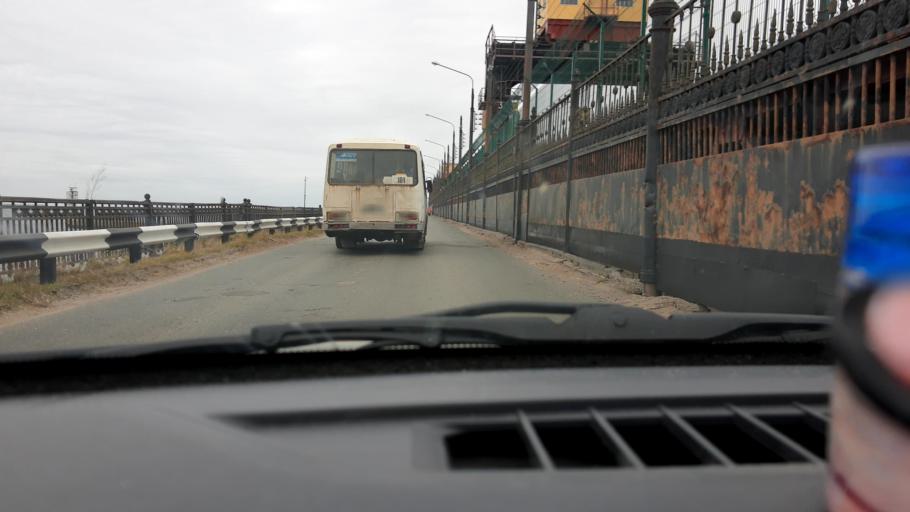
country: RU
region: Nizjnij Novgorod
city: Zavolzh'ye
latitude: 56.6528
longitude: 43.3747
